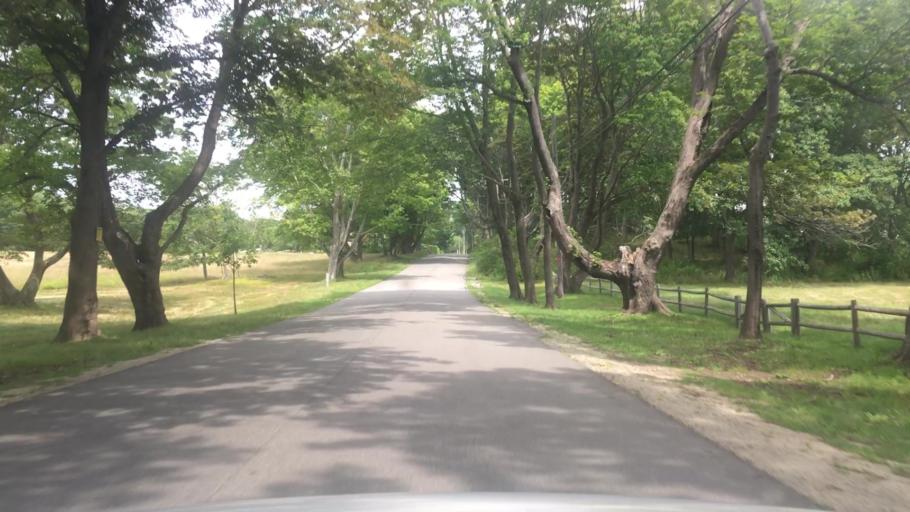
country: US
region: Maine
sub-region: Cumberland County
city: Scarborough
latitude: 43.5600
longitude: -70.2656
